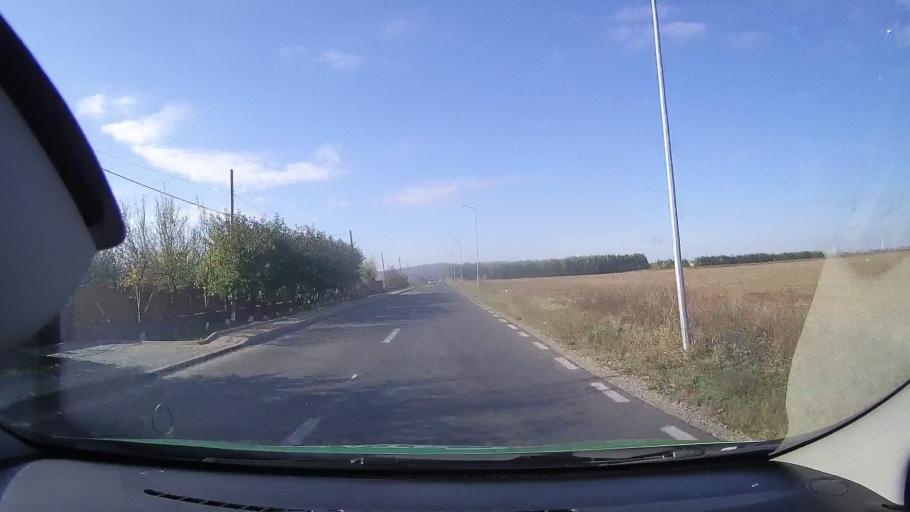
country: RO
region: Tulcea
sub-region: Comuna Valea Nucarilor
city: Valea Nucarilor
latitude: 45.0403
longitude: 28.9232
